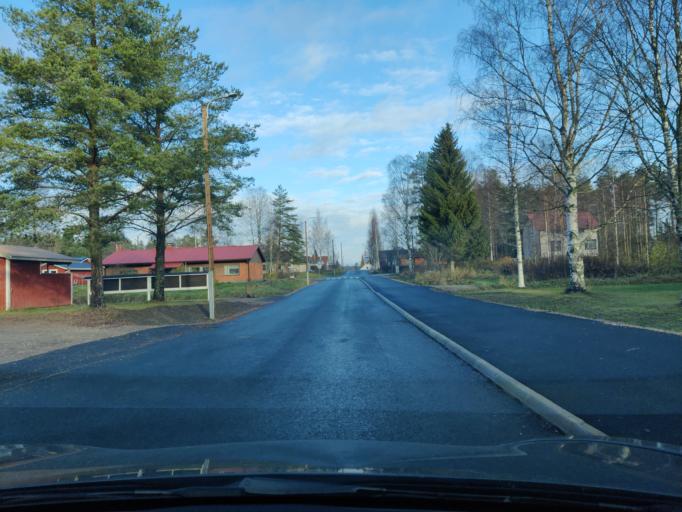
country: FI
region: Northern Savo
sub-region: Ylae-Savo
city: Kiuruvesi
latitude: 63.6469
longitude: 26.6321
